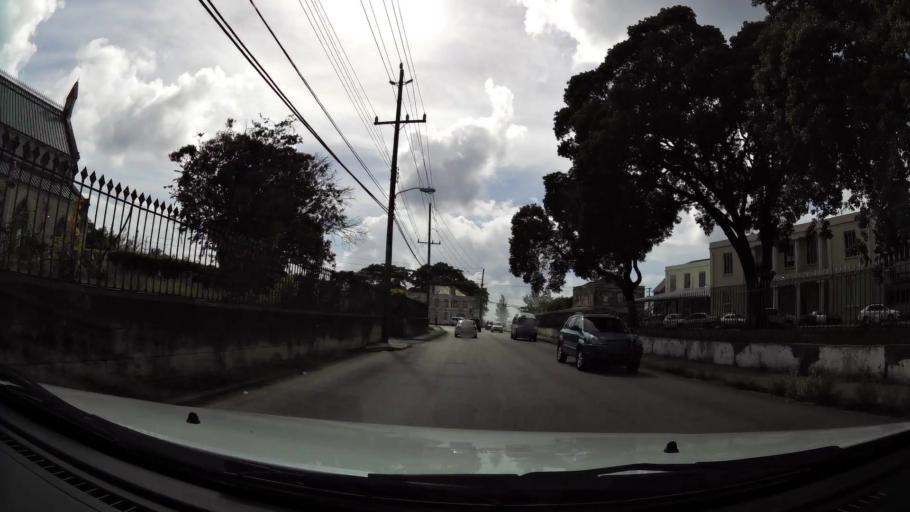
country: BB
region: Saint Michael
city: Bridgetown
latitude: 13.0923
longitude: -59.6091
